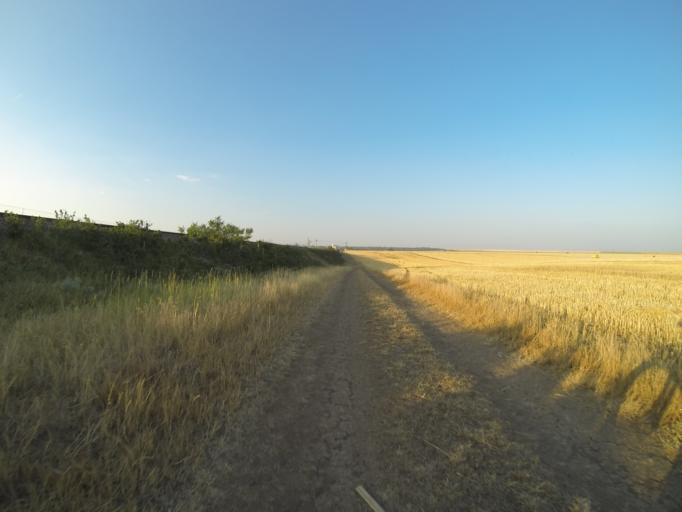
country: RO
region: Dolj
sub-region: Comuna Ceratu
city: Ceratu
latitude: 44.0725
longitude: 23.7087
